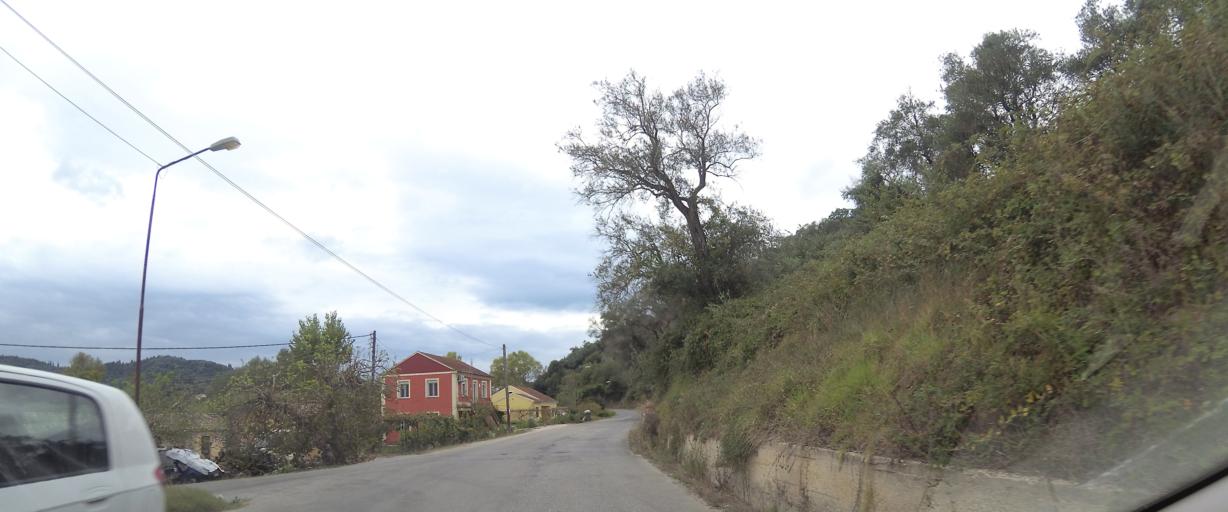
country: GR
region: Ionian Islands
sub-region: Nomos Kerkyras
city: Agios Georgis
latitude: 39.7704
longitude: 19.6997
